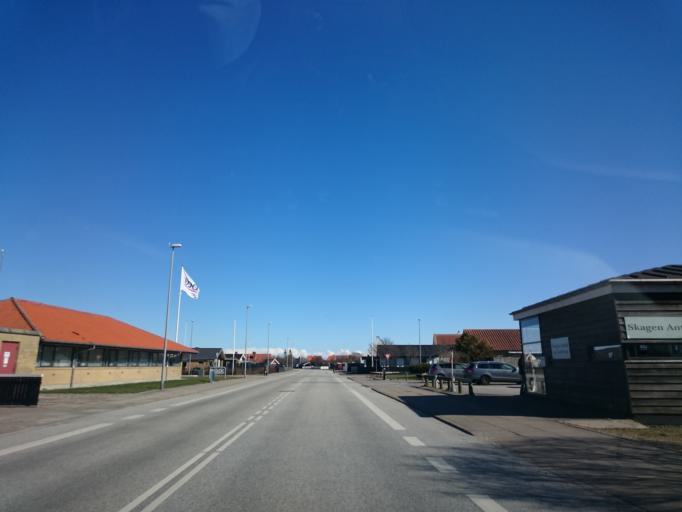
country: DK
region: North Denmark
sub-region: Frederikshavn Kommune
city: Skagen
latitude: 57.7274
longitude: 10.5929
